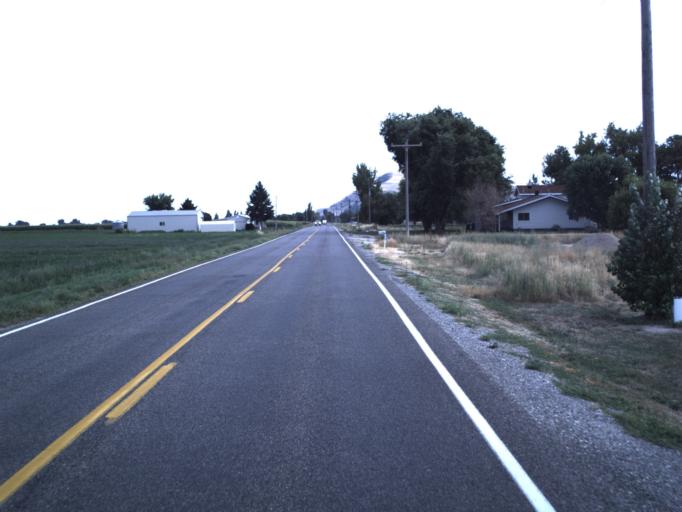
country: US
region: Utah
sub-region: Cache County
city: Lewiston
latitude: 41.9494
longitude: -111.9539
